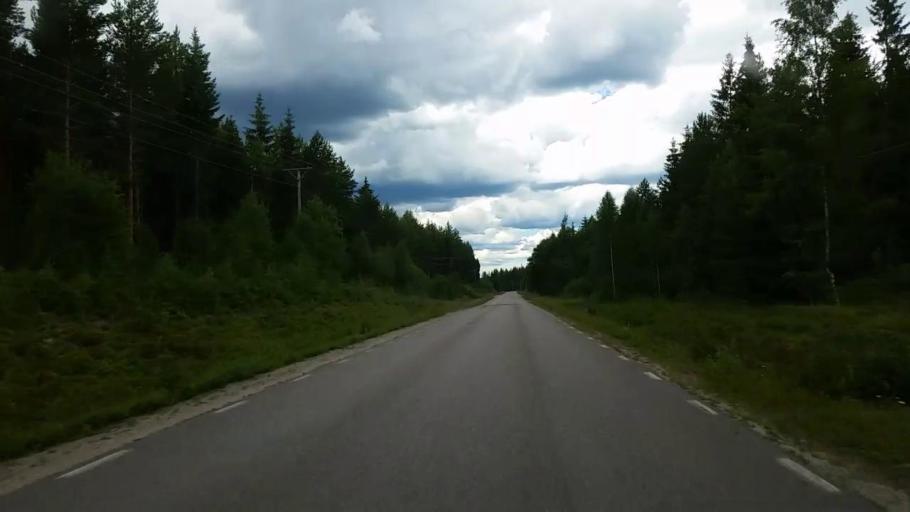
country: SE
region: Gaevleborg
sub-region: Ovanakers Kommun
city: Edsbyn
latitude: 61.4278
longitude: 15.8992
